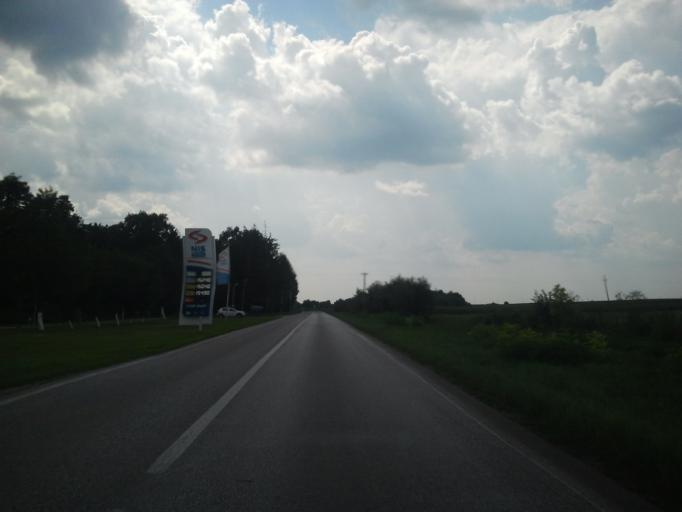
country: RS
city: Celarevo
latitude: 45.2543
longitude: 19.4886
